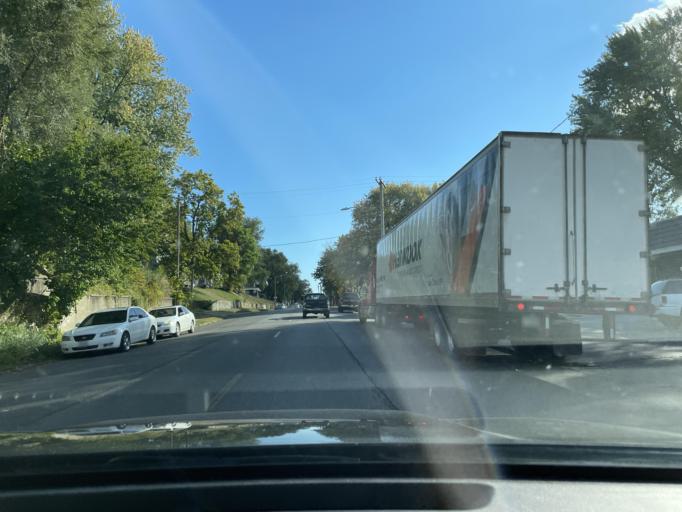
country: US
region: Kansas
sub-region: Doniphan County
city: Elwood
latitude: 39.7184
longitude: -94.8623
